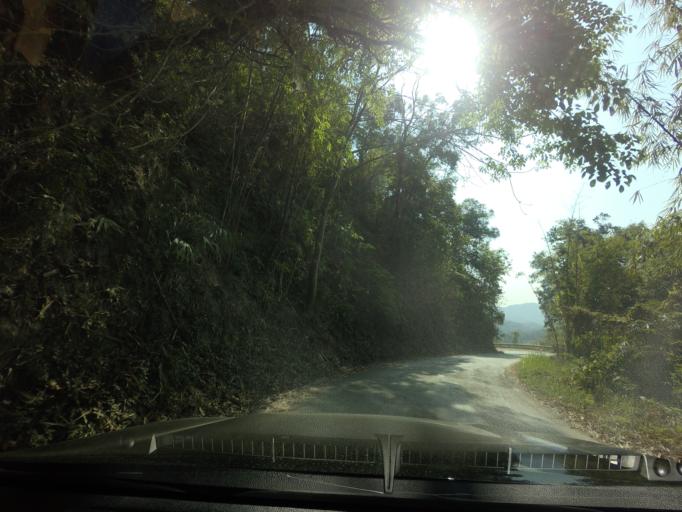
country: TH
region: Kanchanaburi
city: Thong Pha Phum
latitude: 14.7012
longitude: 98.4607
